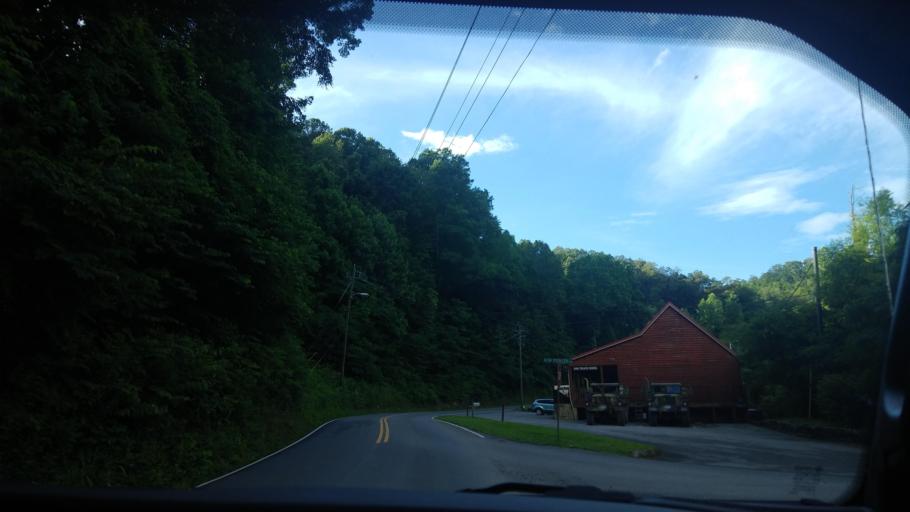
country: US
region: Tennessee
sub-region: Sevier County
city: Pigeon Forge
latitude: 35.7623
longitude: -83.5616
